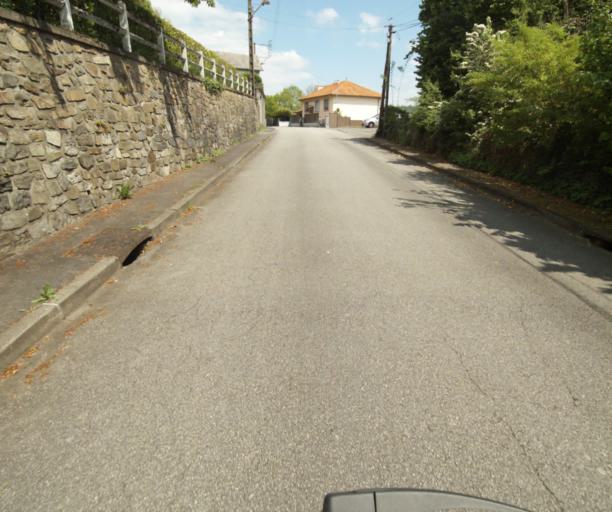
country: FR
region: Limousin
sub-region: Departement de la Correze
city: Tulle
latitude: 45.2733
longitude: 1.7689
